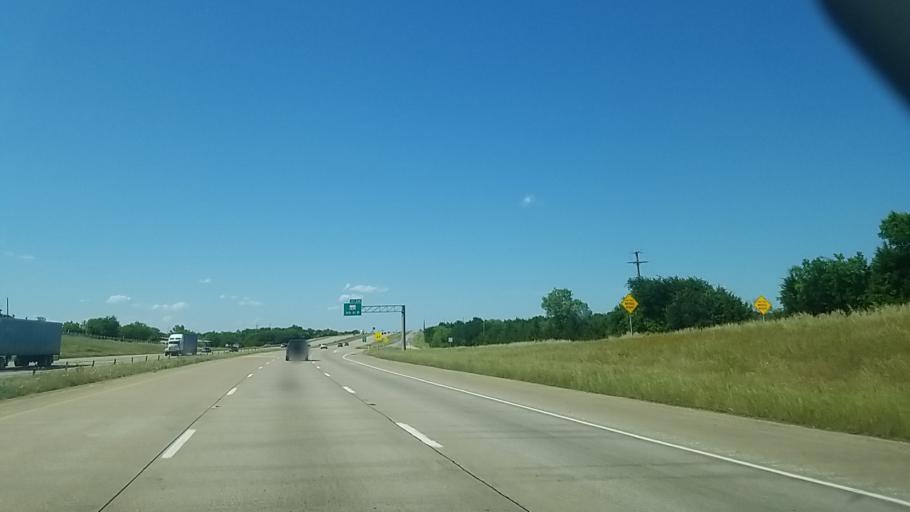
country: US
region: Texas
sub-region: Ellis County
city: Ferris
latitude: 32.5151
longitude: -96.6632
